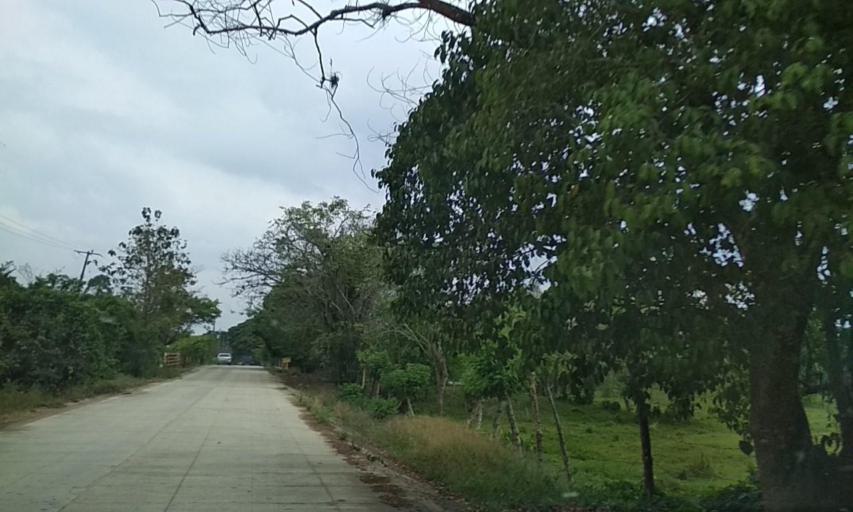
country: MX
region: Tabasco
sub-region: Huimanguillo
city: Francisco Rueda
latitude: 17.6716
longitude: -94.0910
